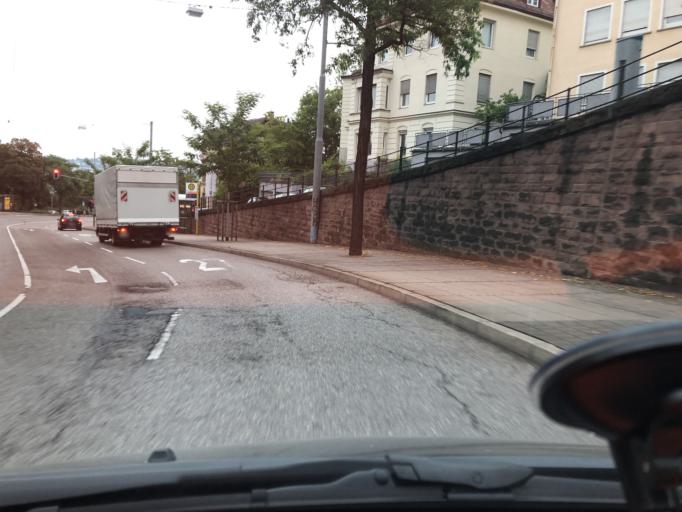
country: DE
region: Baden-Wuerttemberg
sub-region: Regierungsbezirk Stuttgart
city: Stuttgart
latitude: 48.7666
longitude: 9.1836
